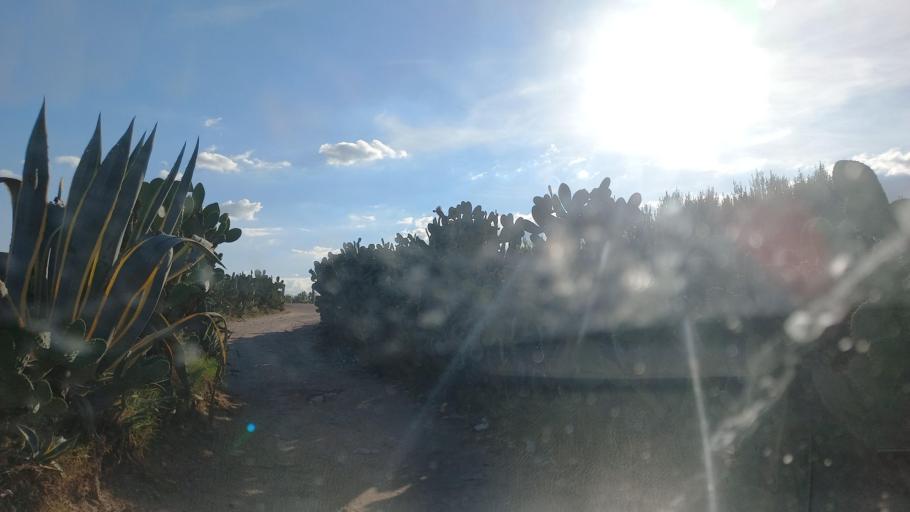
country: TN
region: Al Qasrayn
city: Sbiba
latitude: 35.3800
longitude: 9.0210
